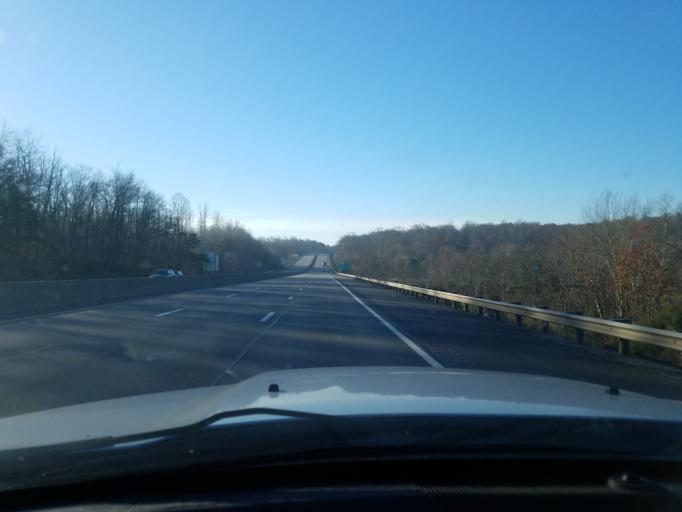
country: US
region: West Virginia
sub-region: Wood County
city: Parkersburg
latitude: 39.2498
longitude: -81.5006
